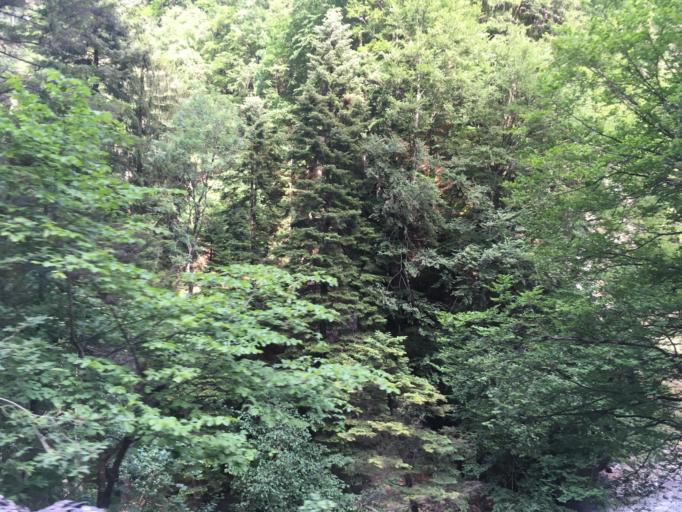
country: CH
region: Saint Gallen
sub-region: Wahlkreis Sarganserland
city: Bad Ragaz
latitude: 46.9792
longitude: 9.4860
